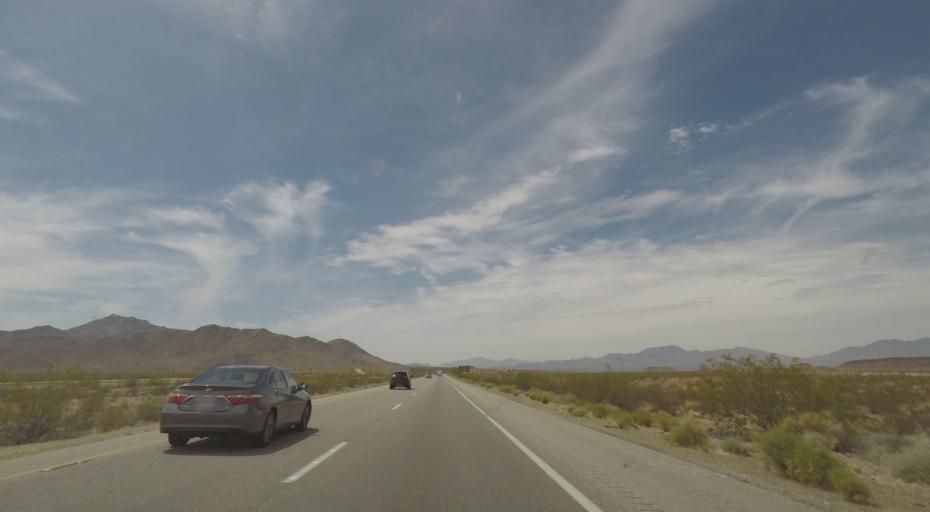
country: US
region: California
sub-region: San Bernardino County
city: Needles
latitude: 34.8020
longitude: -115.3100
